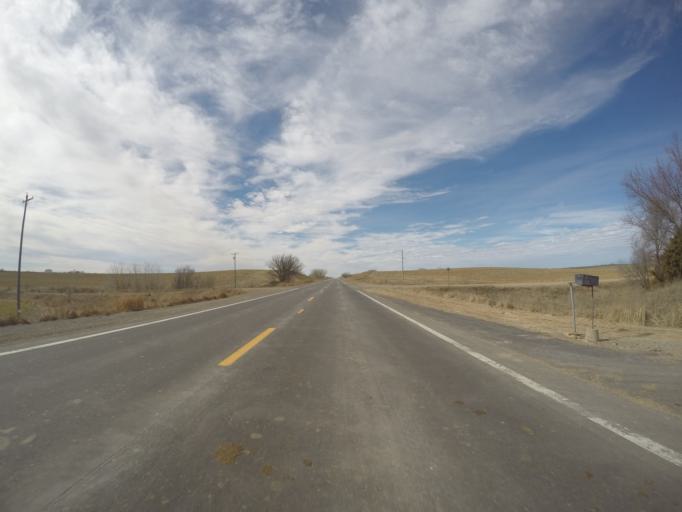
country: US
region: Nebraska
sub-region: Franklin County
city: Franklin
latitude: 40.0969
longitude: -98.8006
